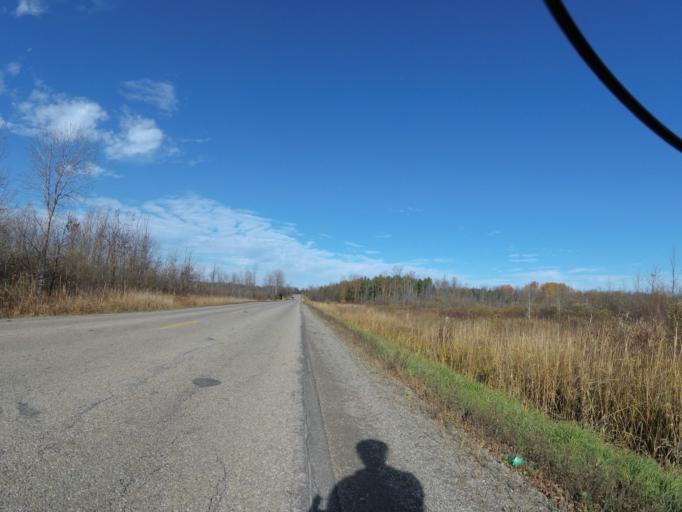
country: CA
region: Ontario
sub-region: Lanark County
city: Smiths Falls
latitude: 44.8318
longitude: -75.9358
